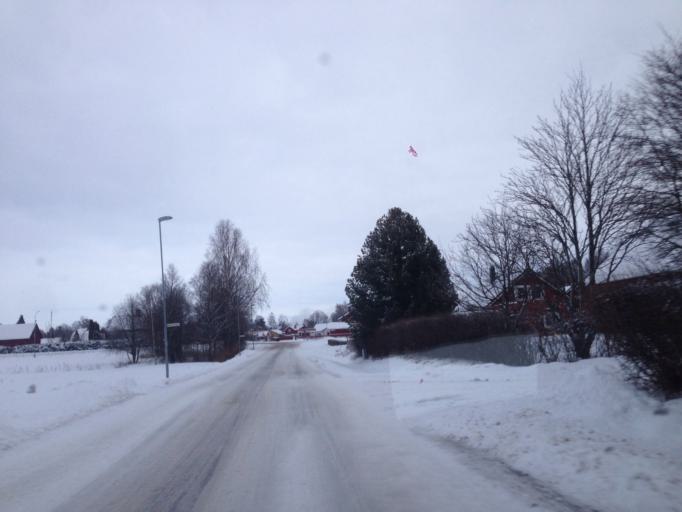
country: SE
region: Dalarna
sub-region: Mora Kommun
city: Mora
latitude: 61.0084
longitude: 14.5827
